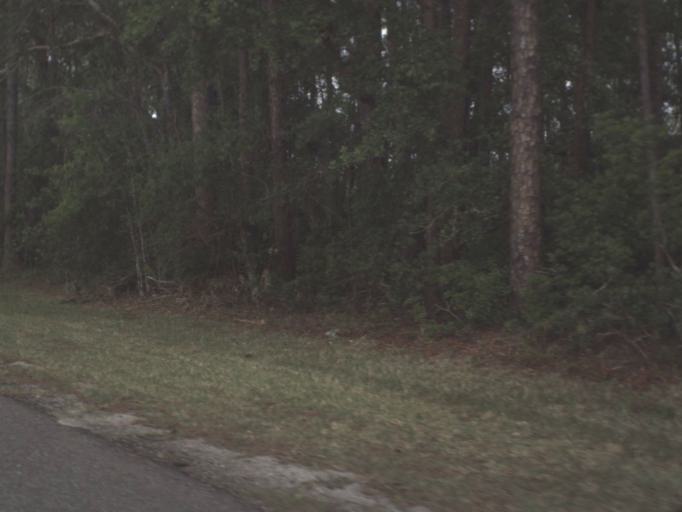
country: US
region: Florida
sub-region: Volusia County
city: Pierson
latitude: 29.2966
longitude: -81.3231
